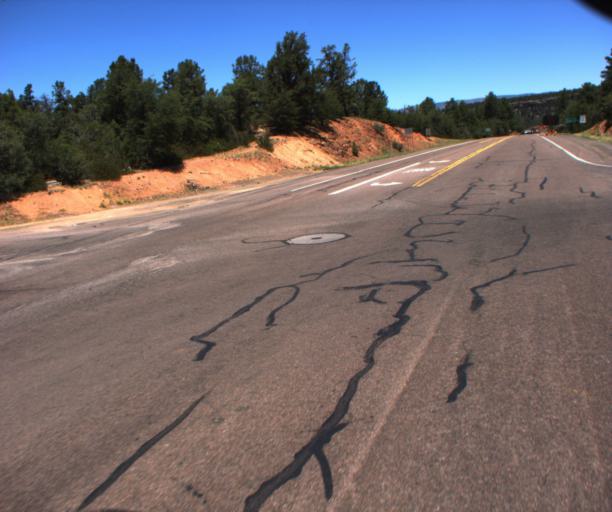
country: US
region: Arizona
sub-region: Gila County
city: Payson
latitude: 34.2680
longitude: -111.3220
